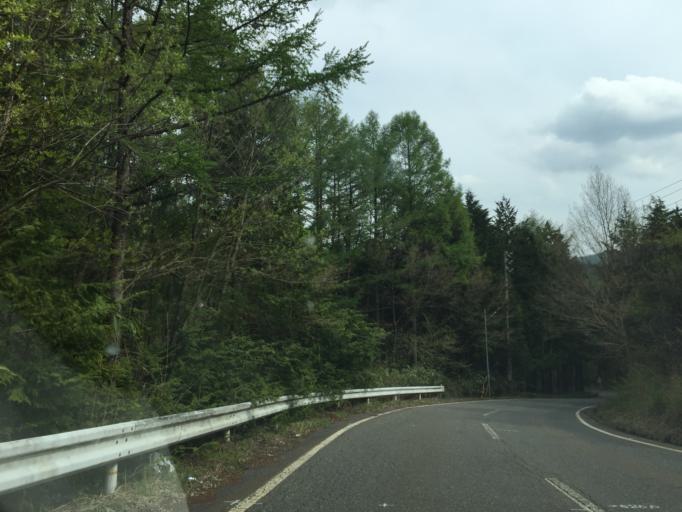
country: JP
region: Gifu
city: Nakatsugawa
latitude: 35.2974
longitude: 137.6795
